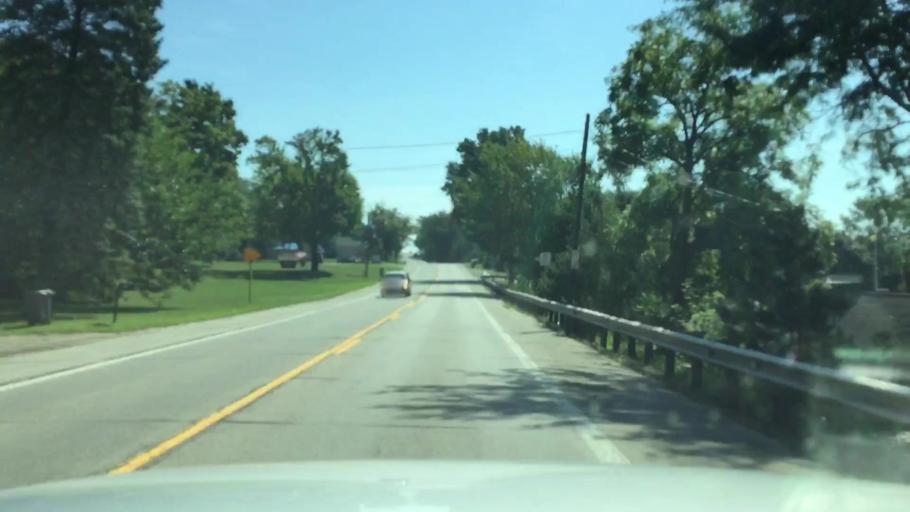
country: US
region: Michigan
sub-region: Lenawee County
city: Manitou Beach-Devils Lake
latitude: 42.0065
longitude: -84.2882
